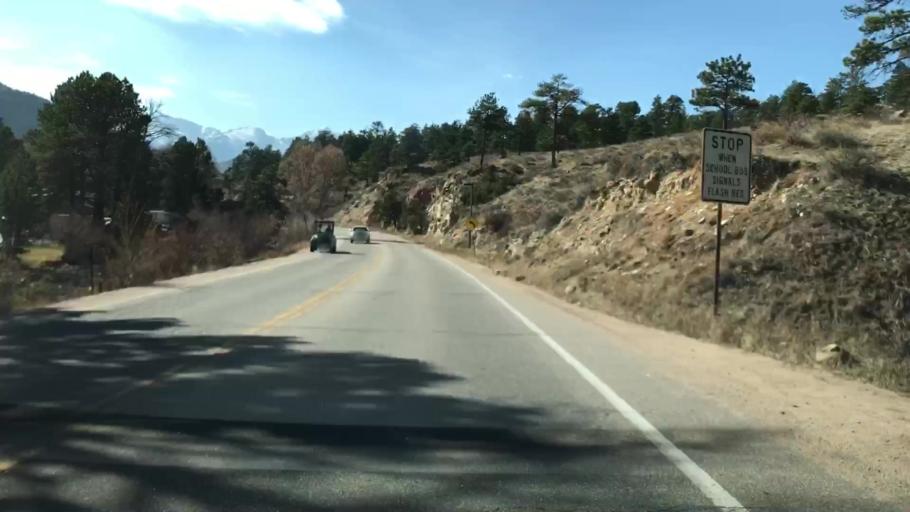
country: US
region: Colorado
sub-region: Larimer County
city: Estes Park
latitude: 40.3722
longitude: -105.5266
